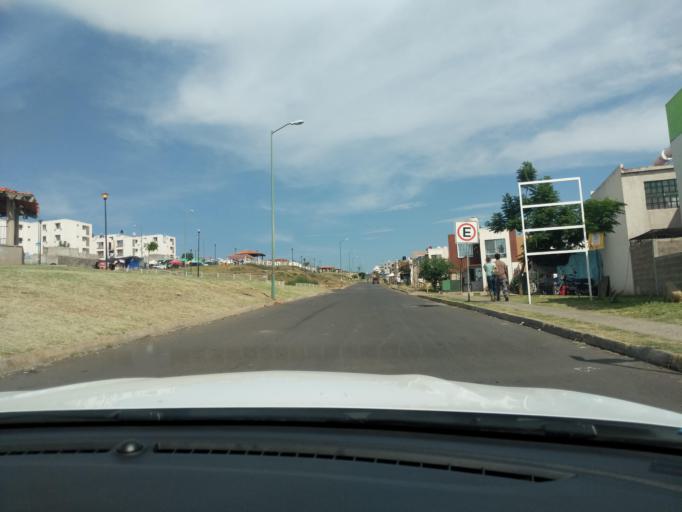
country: MX
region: Jalisco
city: San Jose del Castillo
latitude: 20.5208
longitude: -103.2278
